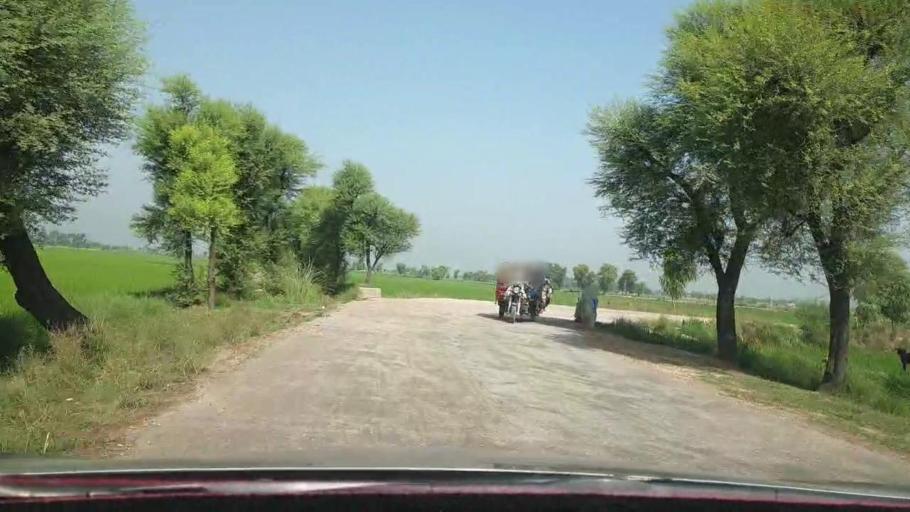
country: PK
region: Sindh
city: Warah
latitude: 27.4723
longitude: 67.8318
